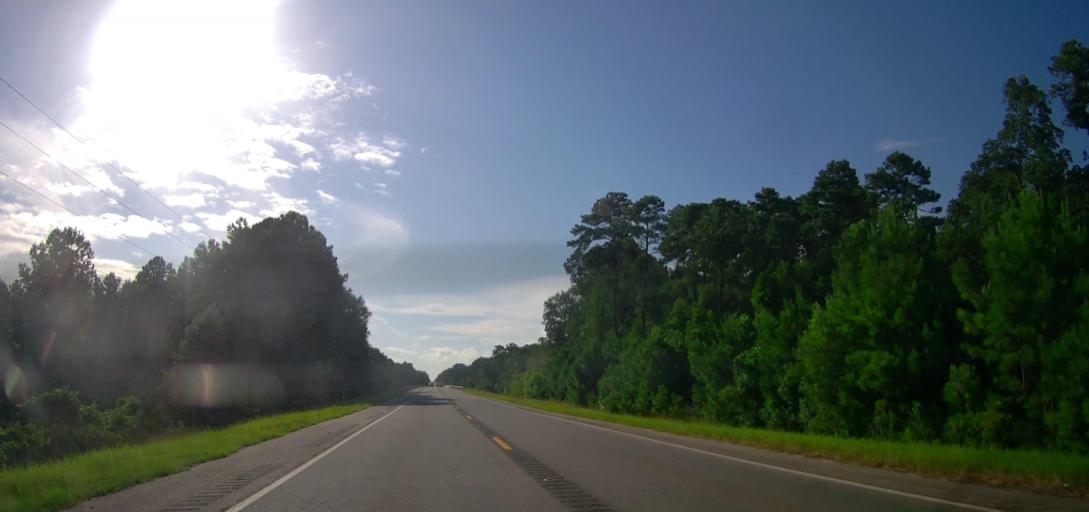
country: US
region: Georgia
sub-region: Coffee County
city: Douglas
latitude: 31.4668
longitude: -82.7623
